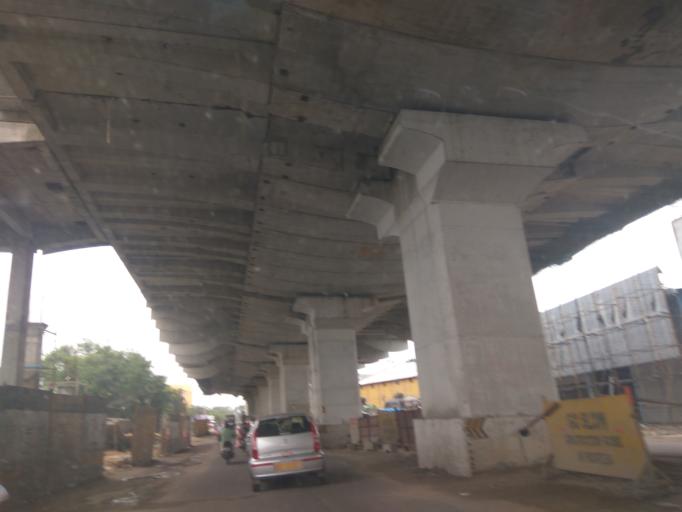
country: IN
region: Telangana
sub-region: Hyderabad
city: Malkajgiri
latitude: 17.4260
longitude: 78.5020
